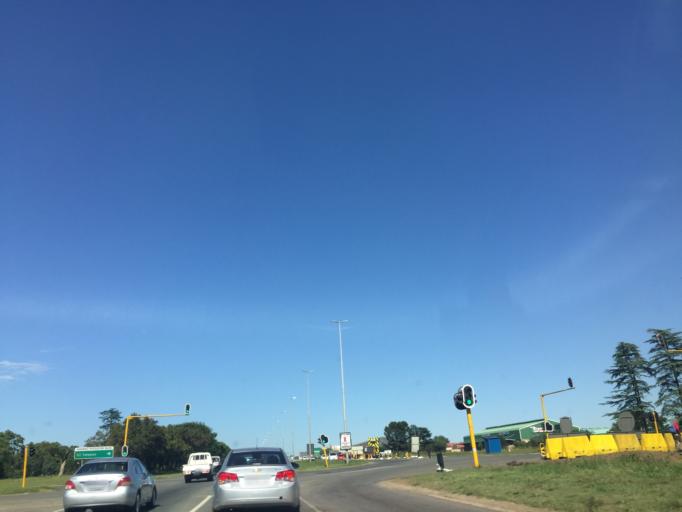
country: ZA
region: Gauteng
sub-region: Sedibeng District Municipality
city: Vanderbijlpark
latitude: -26.7080
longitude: 27.8606
